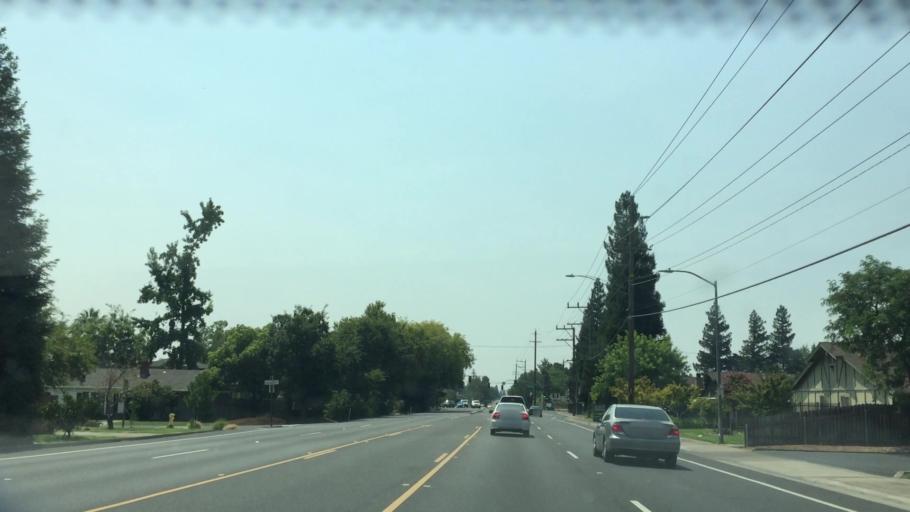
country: US
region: California
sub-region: Sacramento County
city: Arden-Arcade
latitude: 38.6122
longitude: -121.3646
